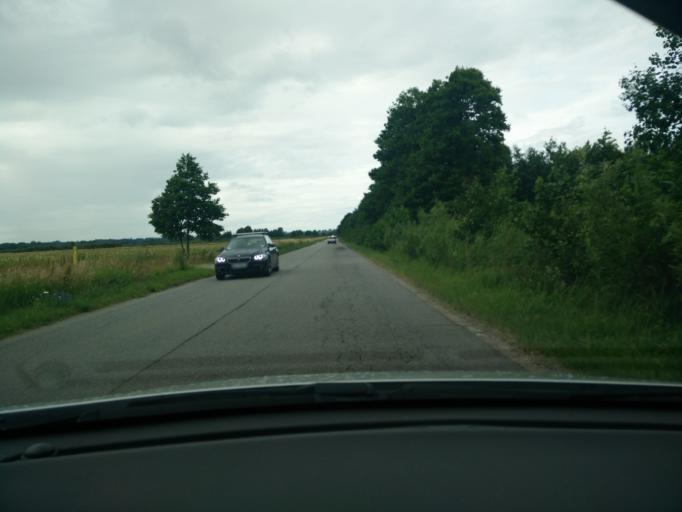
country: PL
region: Pomeranian Voivodeship
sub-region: Powiat pucki
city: Kosakowo
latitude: 54.6097
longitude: 18.4513
